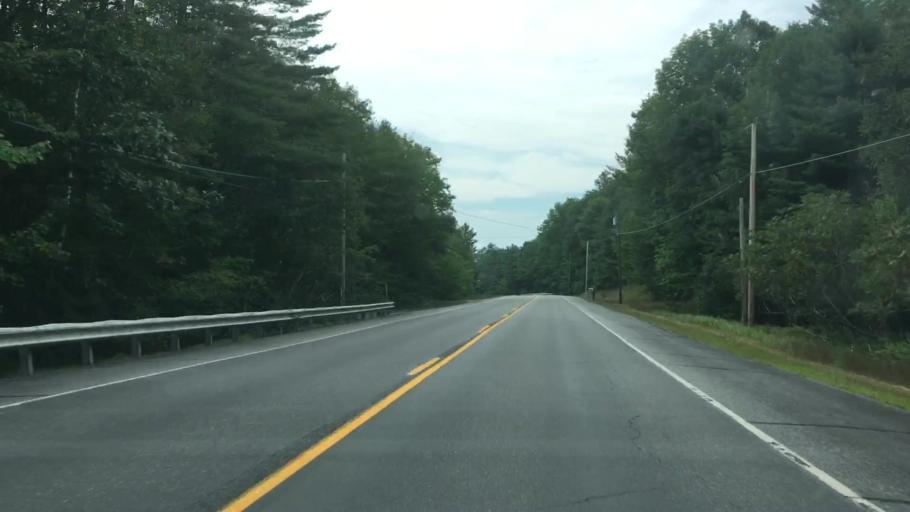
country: US
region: Maine
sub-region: Oxford County
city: Bethel
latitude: 44.4871
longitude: -70.7675
